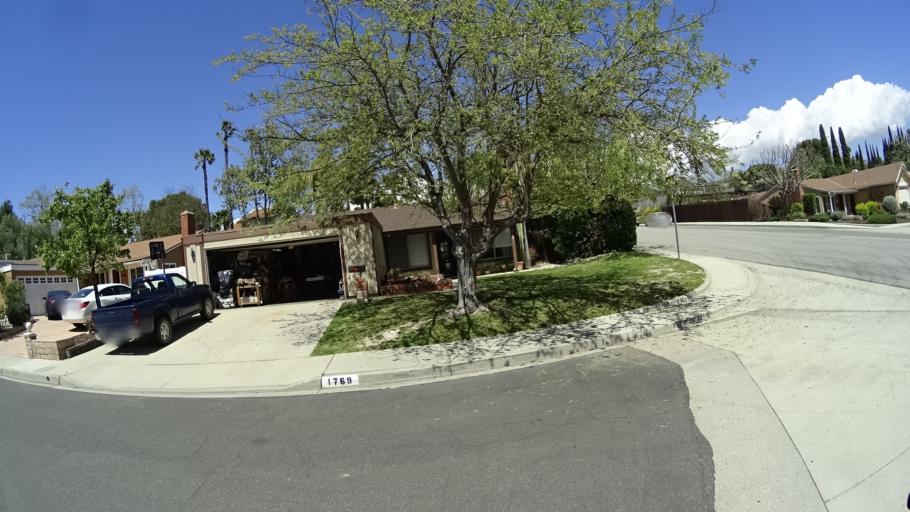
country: US
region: California
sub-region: Ventura County
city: Thousand Oaks
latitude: 34.2139
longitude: -118.8460
